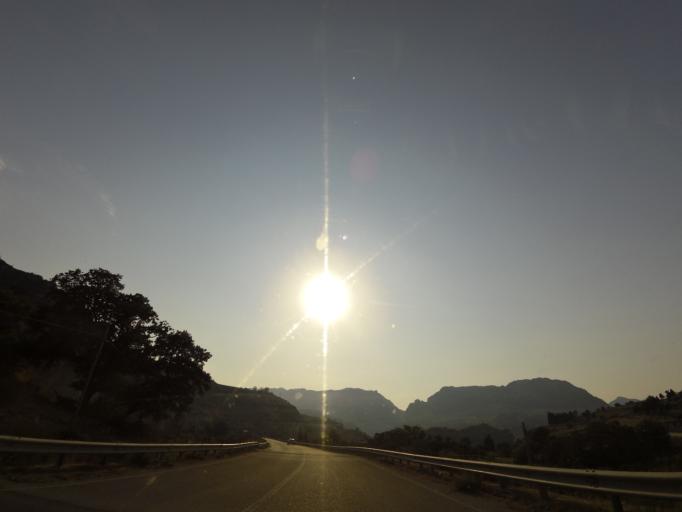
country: IT
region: Calabria
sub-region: Provincia di Reggio Calabria
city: Stilo
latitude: 38.4659
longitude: 16.4942
